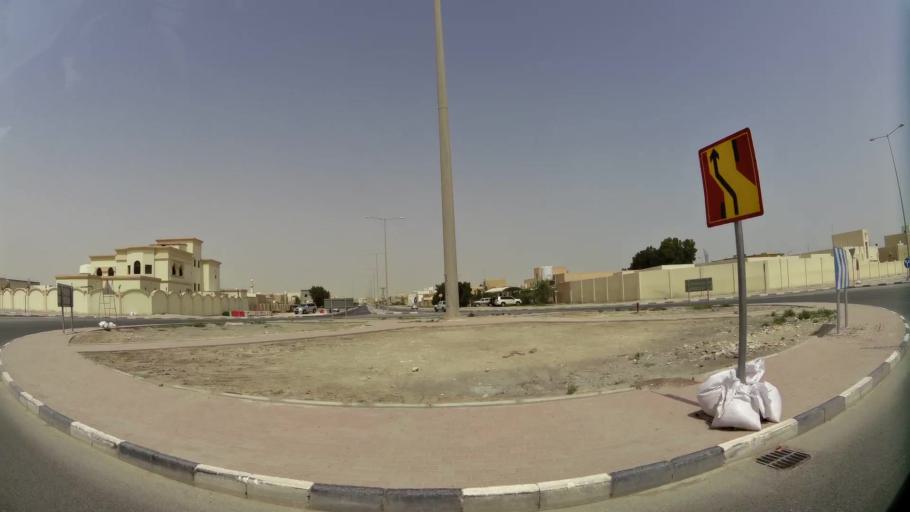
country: QA
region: Baladiyat ar Rayyan
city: Ar Rayyan
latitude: 25.2396
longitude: 51.4204
